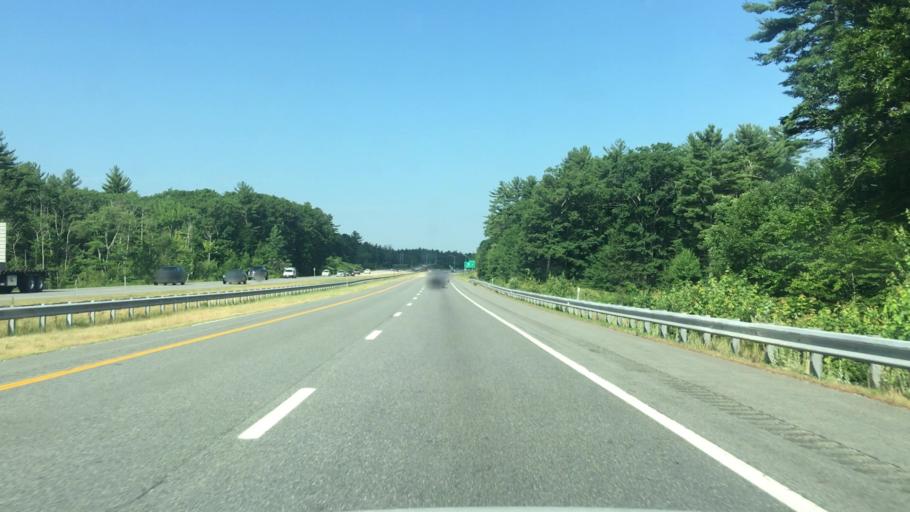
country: US
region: New Hampshire
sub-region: Rockingham County
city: Exeter
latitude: 43.0030
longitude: -70.9630
